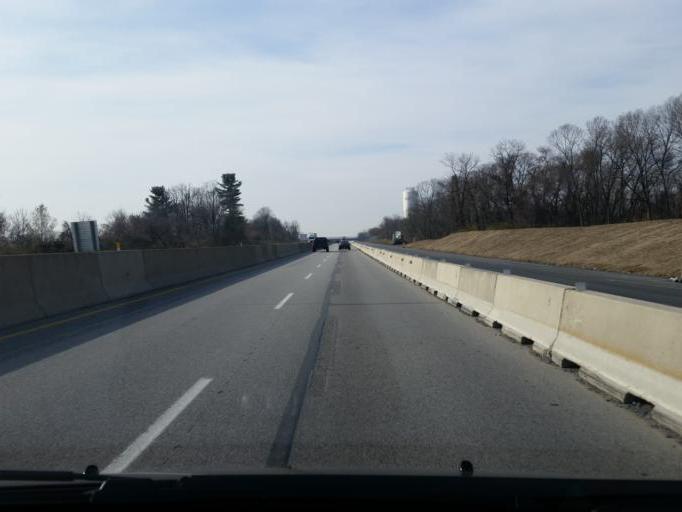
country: US
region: Pennsylvania
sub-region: Cumberland County
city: Schlusser
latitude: 40.2256
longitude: -77.1679
